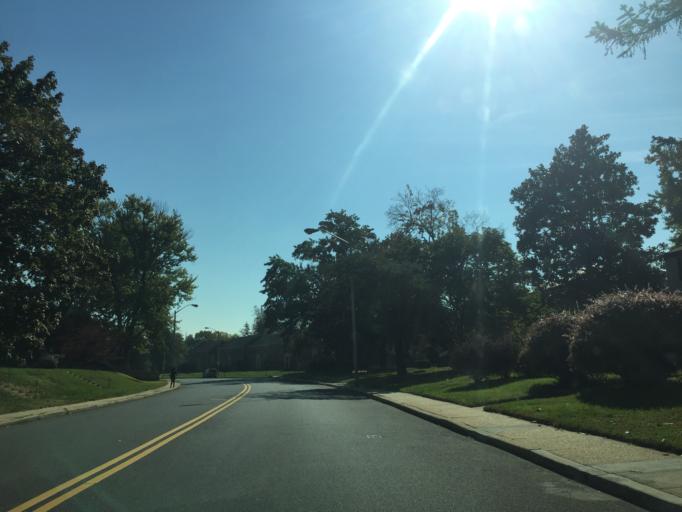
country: US
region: Maryland
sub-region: Baltimore County
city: Towson
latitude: 39.3604
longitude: -76.6011
